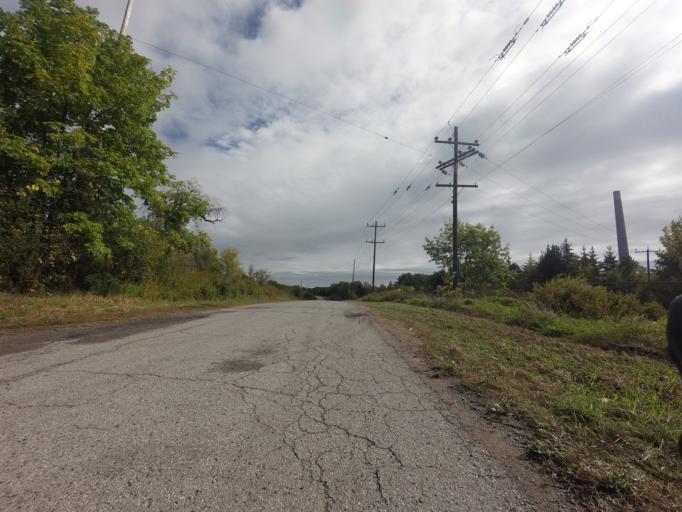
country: CA
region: Ontario
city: Cobourg
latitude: 43.9283
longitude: -78.3994
